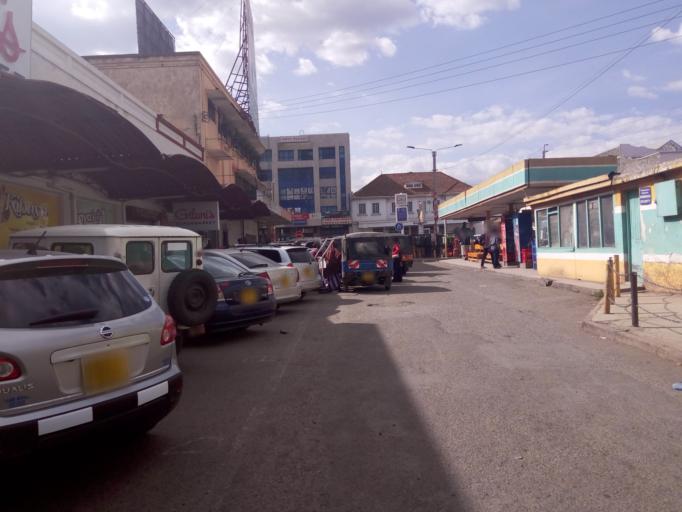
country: KE
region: Nakuru
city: Nakuru
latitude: -0.2852
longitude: 36.0715
